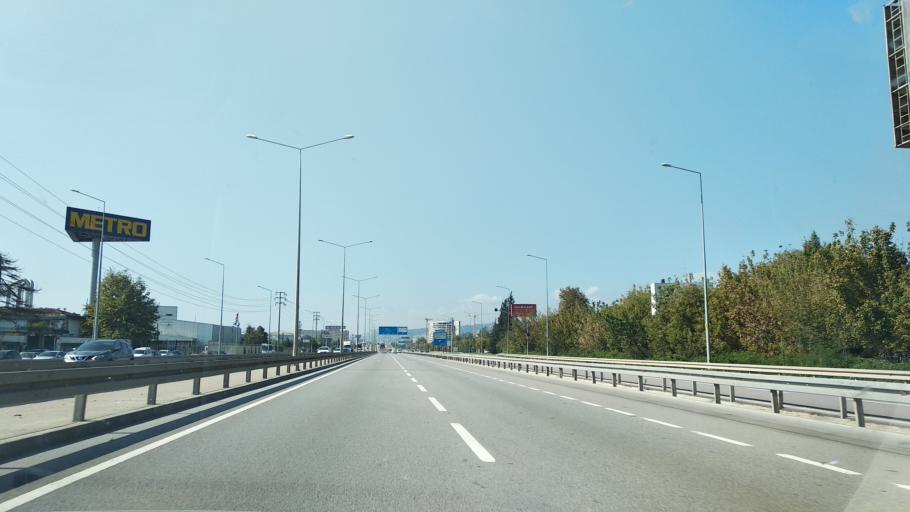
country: TR
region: Kocaeli
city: Kosekoy
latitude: 40.7573
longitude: 29.9966
